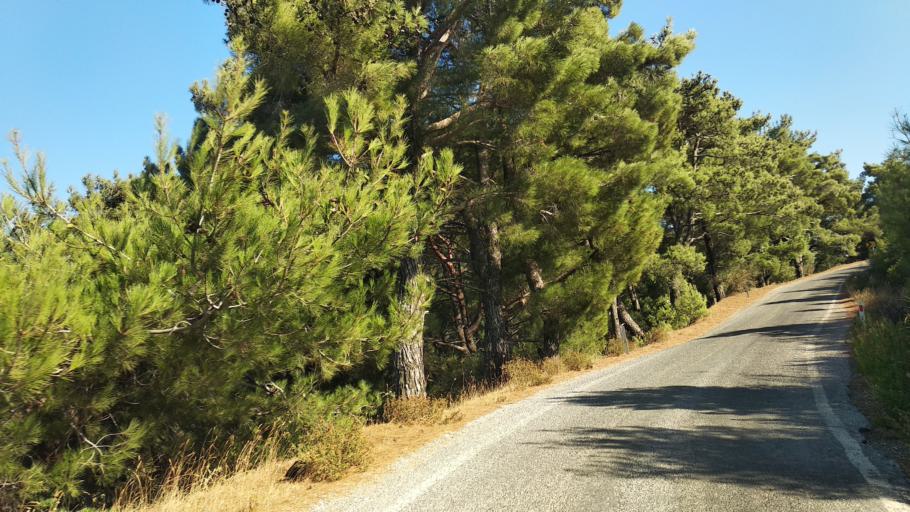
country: TR
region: Izmir
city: Gaziemir
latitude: 38.3270
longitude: 26.9555
